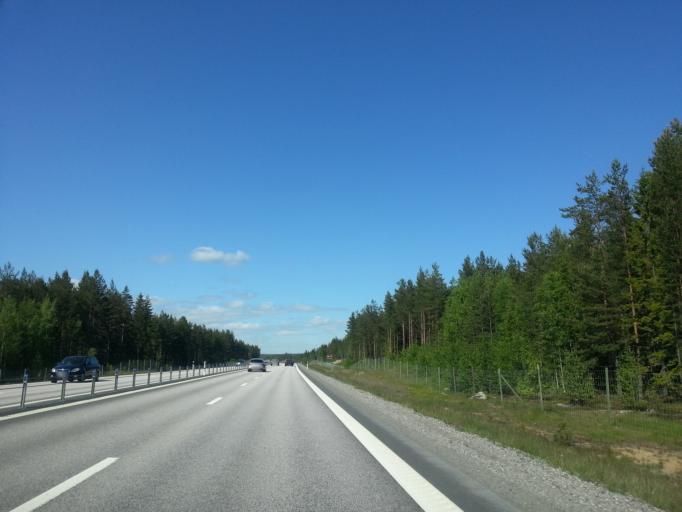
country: SE
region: Gaevleborg
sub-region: Hudiksvalls Kommun
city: Iggesund
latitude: 61.5613
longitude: 16.9744
